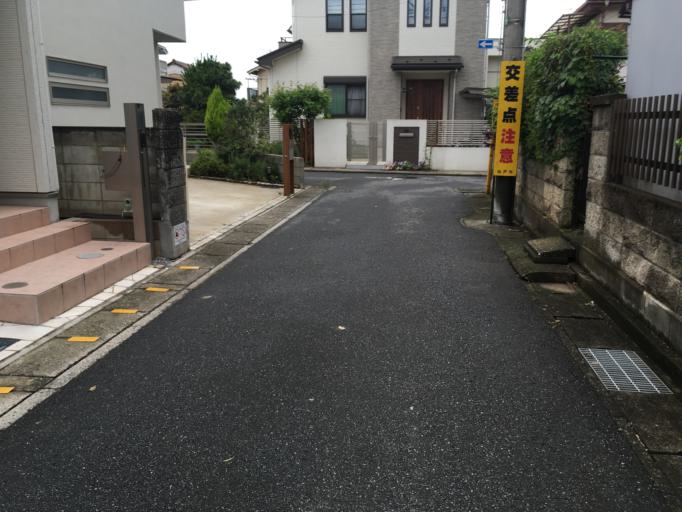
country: JP
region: Chiba
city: Matsudo
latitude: 35.7875
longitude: 139.9227
